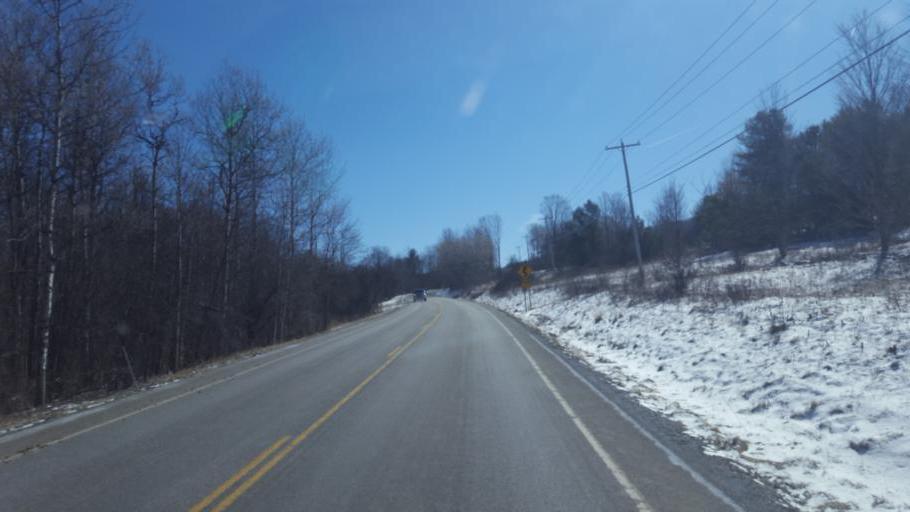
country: US
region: New York
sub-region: Allegany County
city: Andover
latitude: 42.0721
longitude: -77.8463
